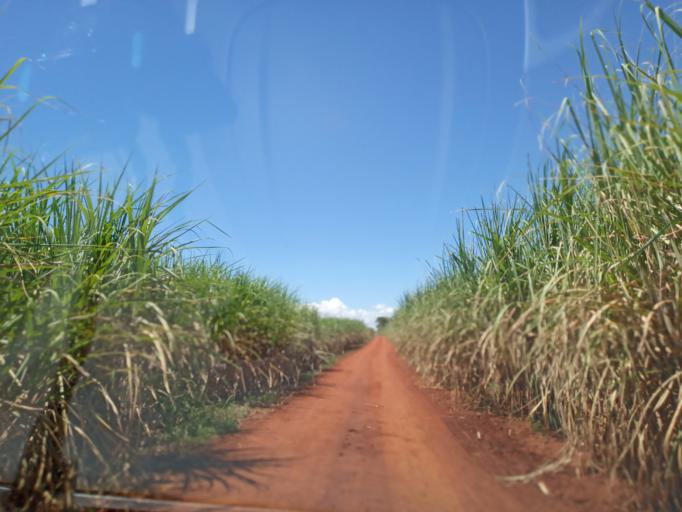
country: BR
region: Goias
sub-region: Itumbiara
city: Itumbiara
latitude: -18.4067
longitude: -49.1279
